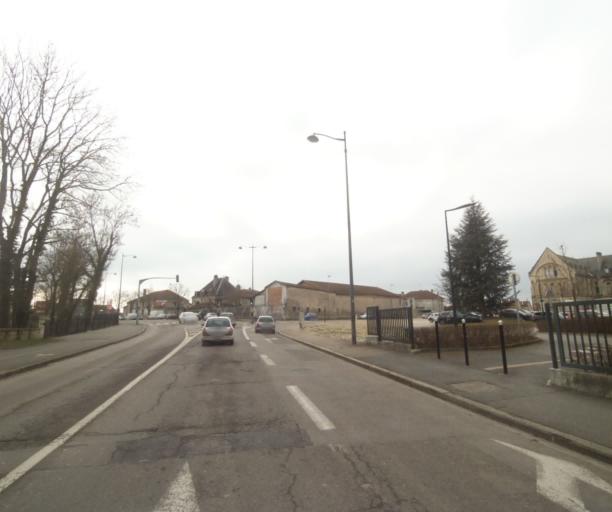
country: FR
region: Champagne-Ardenne
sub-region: Departement de la Haute-Marne
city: Saint-Dizier
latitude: 48.6326
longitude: 4.9544
